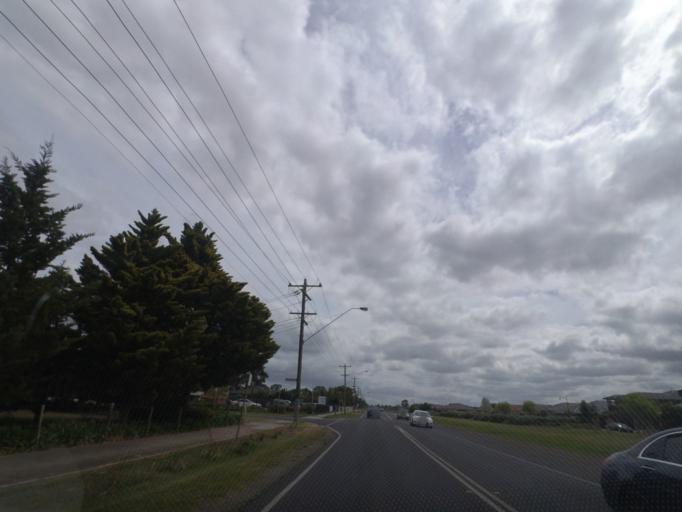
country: AU
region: Victoria
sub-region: Wyndham
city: Hoppers Crossing
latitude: -37.8497
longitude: 144.6986
